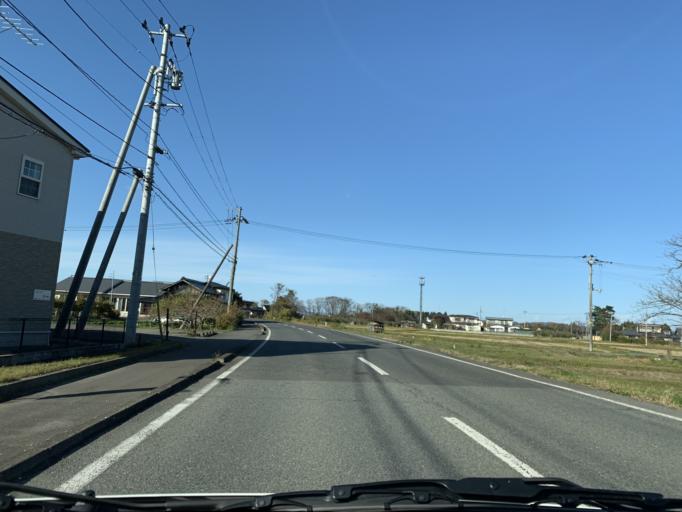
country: JP
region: Iwate
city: Mizusawa
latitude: 39.1732
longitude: 141.1405
